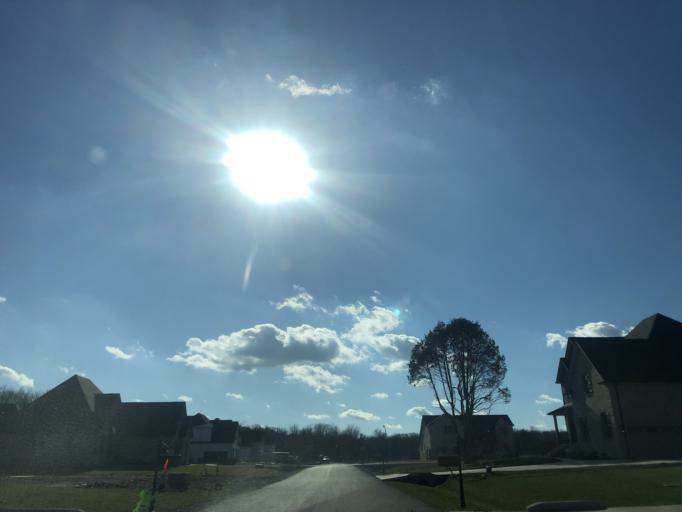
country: US
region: Tennessee
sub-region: Rutherford County
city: Smyrna
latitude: 35.9516
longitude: -86.4180
